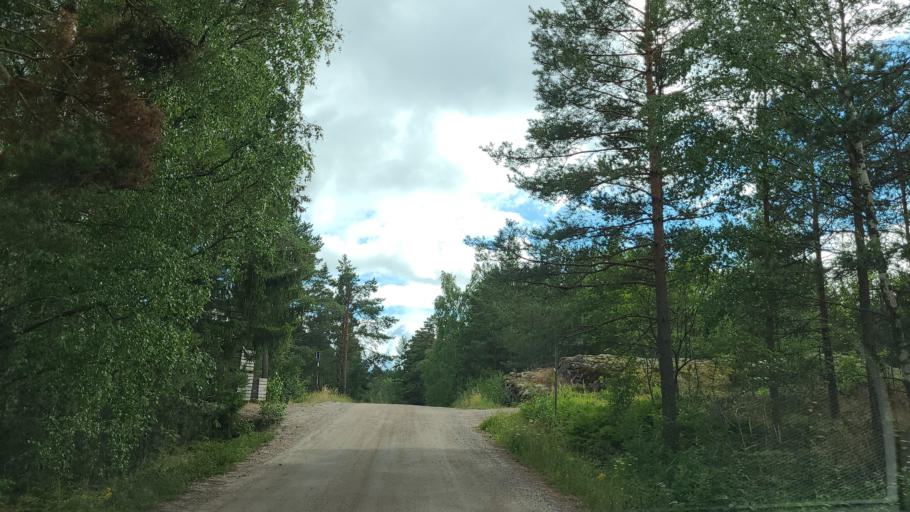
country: FI
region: Varsinais-Suomi
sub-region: Aboland-Turunmaa
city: Nagu
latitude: 60.2028
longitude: 21.7916
